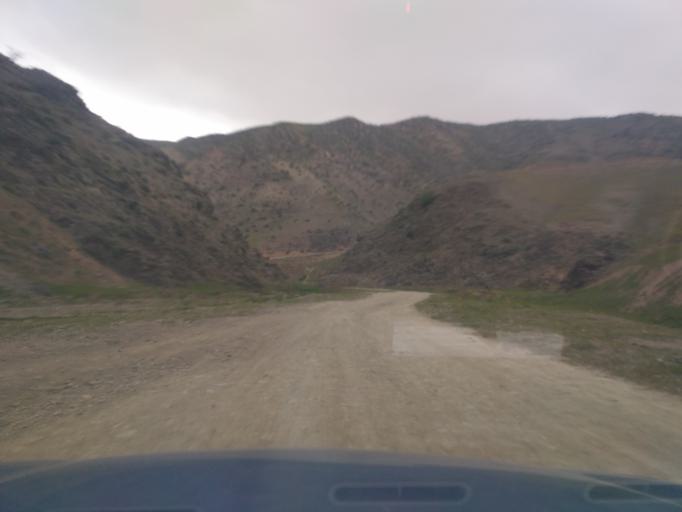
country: UZ
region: Jizzax
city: Zomin
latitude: 39.8557
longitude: 68.3894
